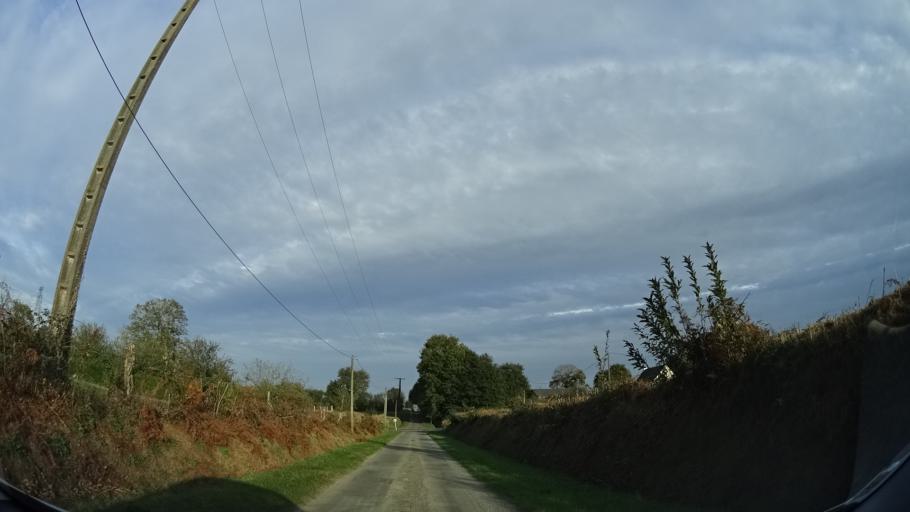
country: FR
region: Brittany
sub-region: Departement d'Ille-et-Vilaine
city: Geveze
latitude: 48.1963
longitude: -1.7957
